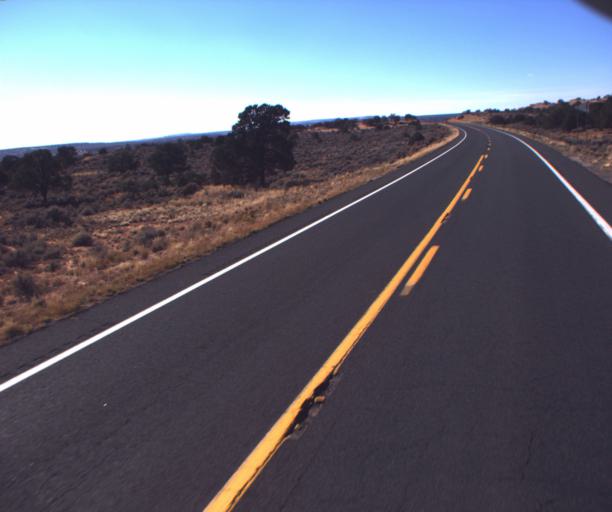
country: US
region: Arizona
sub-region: Coconino County
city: Kaibito
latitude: 36.5616
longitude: -110.7241
